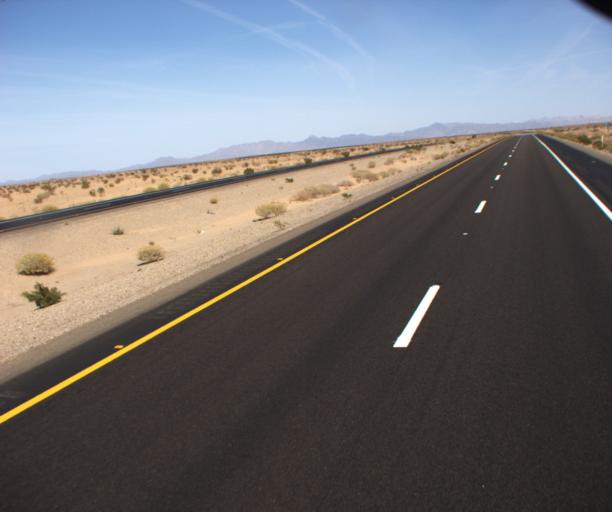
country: US
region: Arizona
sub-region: Yuma County
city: Somerton
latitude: 32.4951
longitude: -114.5821
